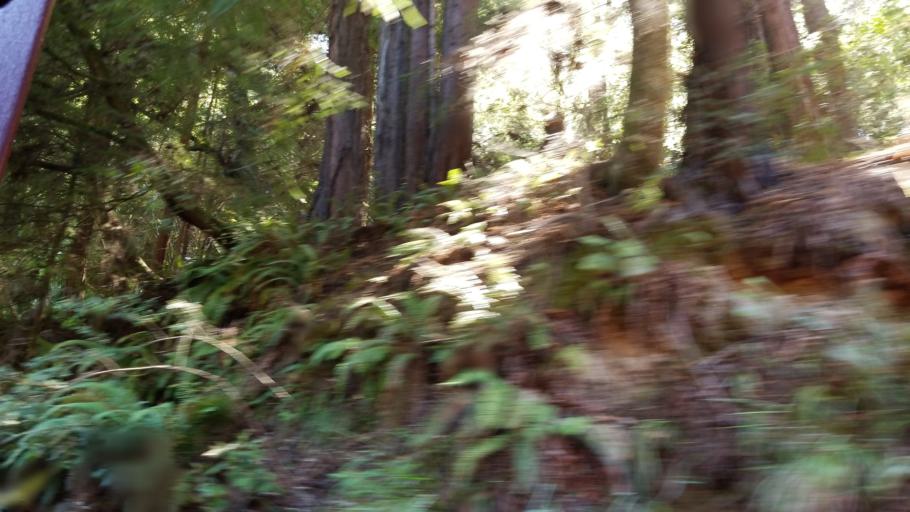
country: US
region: California
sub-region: Mendocino County
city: Fort Bragg
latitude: 39.4488
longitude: -123.7843
